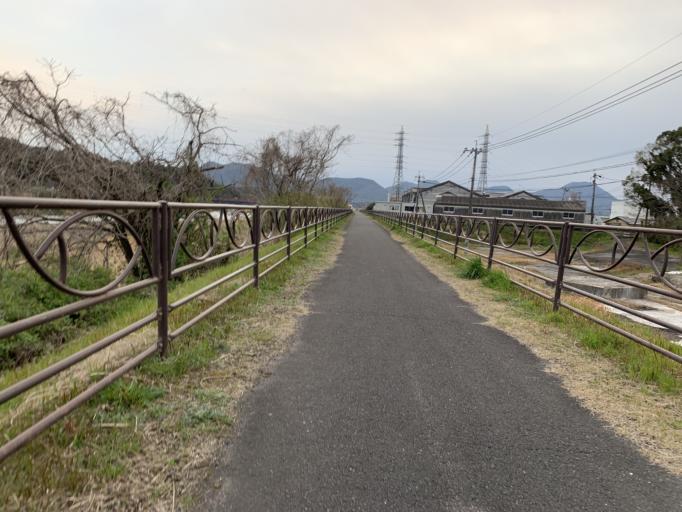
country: JP
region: Oita
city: Bungo-Takada-shi
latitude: 33.5369
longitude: 131.3525
